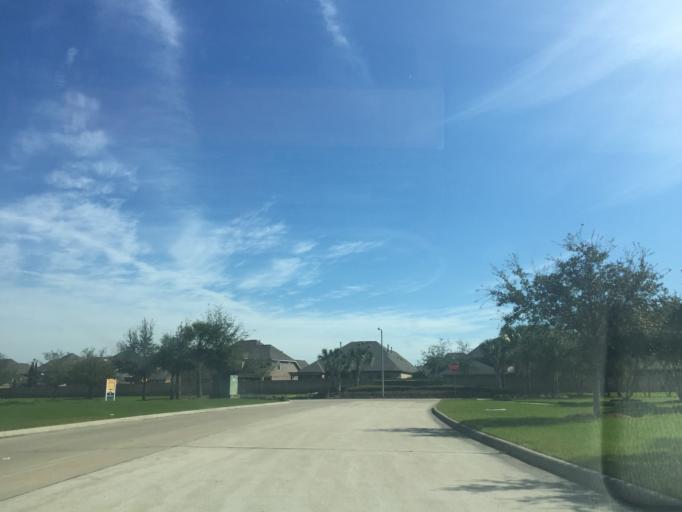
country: US
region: Texas
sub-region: Galveston County
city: Kemah
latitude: 29.5158
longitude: -95.0233
